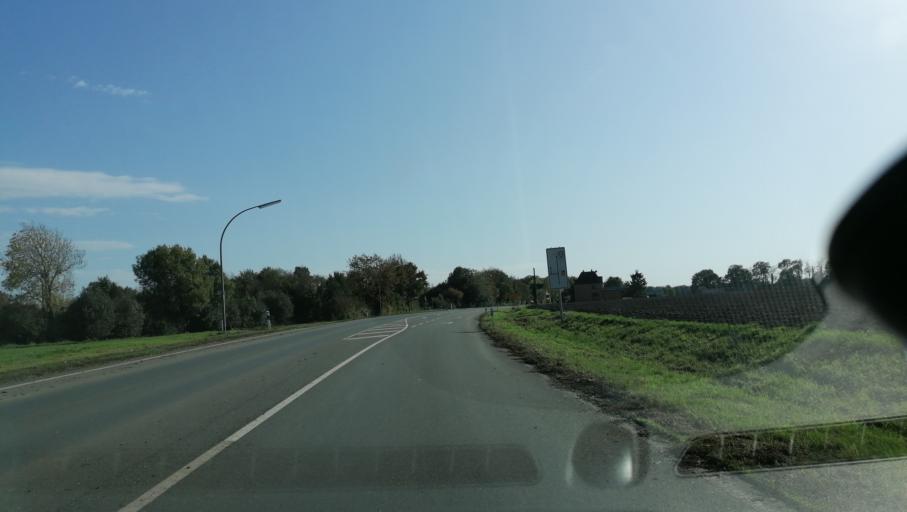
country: DE
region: North Rhine-Westphalia
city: Waltrop
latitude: 51.6175
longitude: 7.4341
